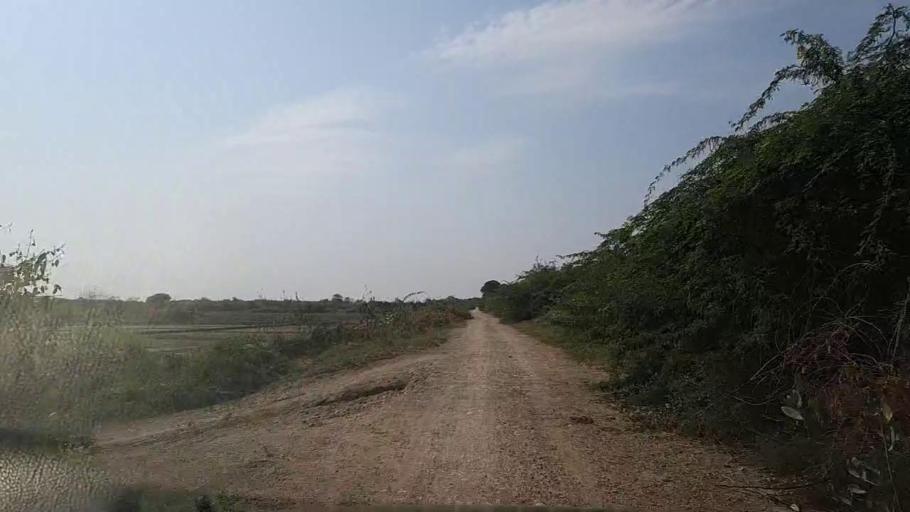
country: PK
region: Sindh
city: Thatta
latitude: 24.7704
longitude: 67.8113
